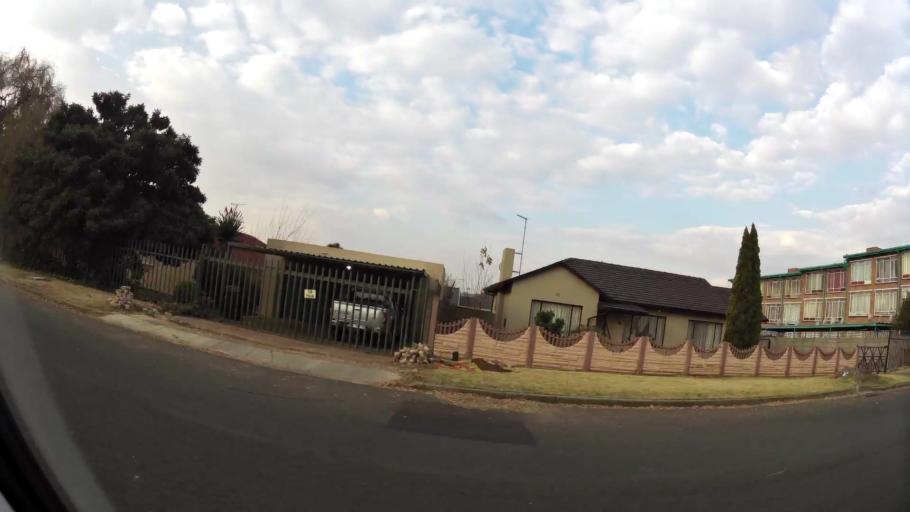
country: ZA
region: Gauteng
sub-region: Ekurhuleni Metropolitan Municipality
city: Germiston
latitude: -26.2503
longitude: 28.1942
